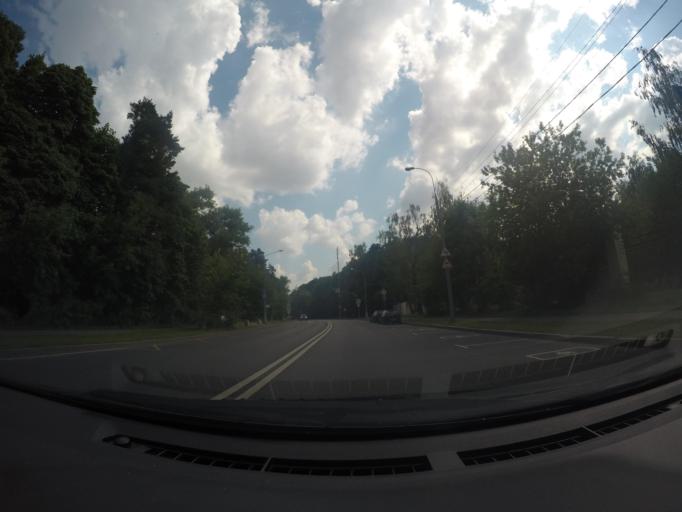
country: RU
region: Moscow
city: Sokol'niki
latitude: 55.8036
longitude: 37.6843
